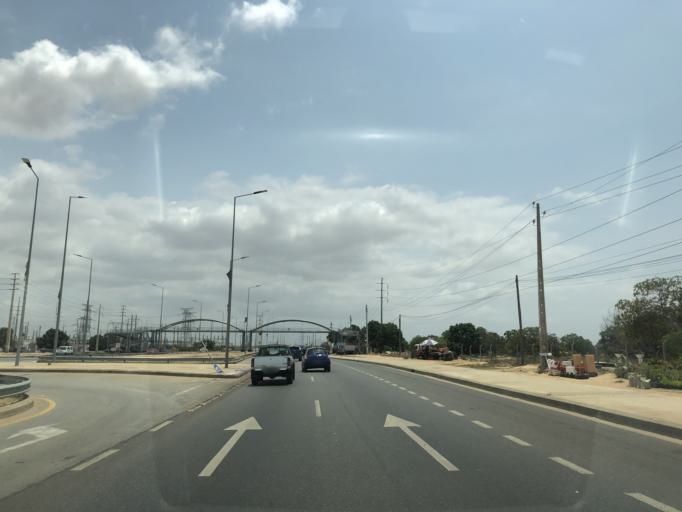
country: AO
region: Luanda
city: Luanda
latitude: -8.9654
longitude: 13.2557
